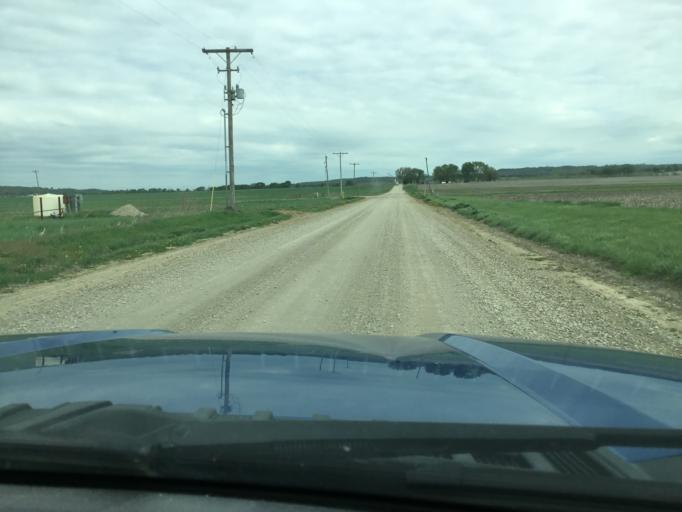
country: US
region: Kansas
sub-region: Douglas County
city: Lawrence
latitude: 39.0138
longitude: -95.2242
